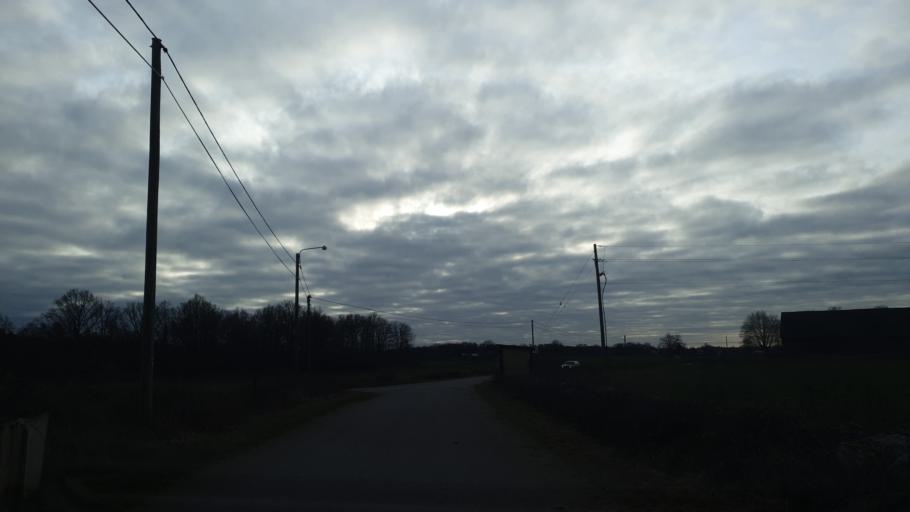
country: SE
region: Kalmar
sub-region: Torsas Kommun
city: Torsas
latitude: 56.3313
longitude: 16.0467
